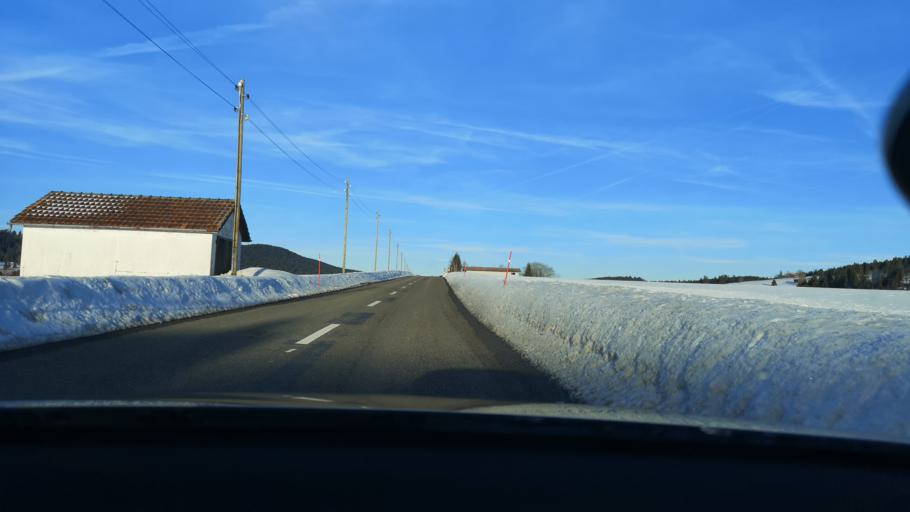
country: CH
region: Neuchatel
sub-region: Val-de-Travers District
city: Fleurier
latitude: 46.9586
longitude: 6.5424
